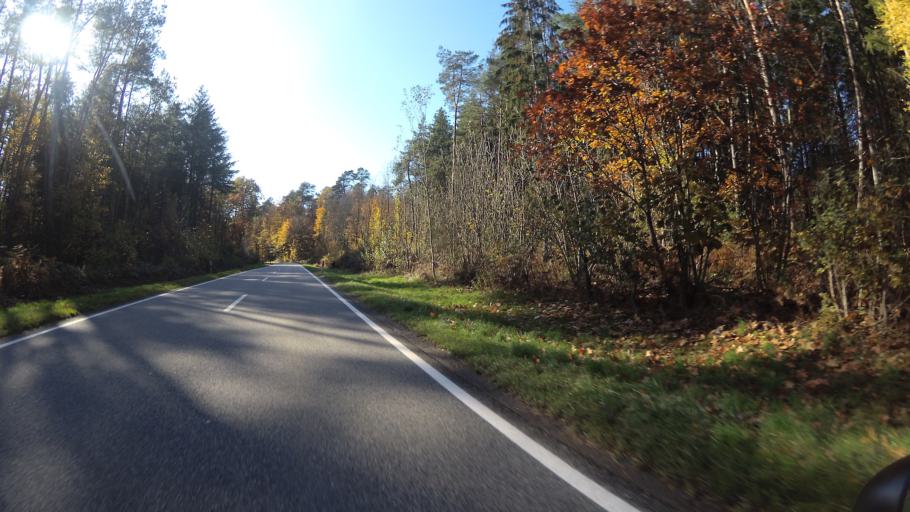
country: DE
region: Saarland
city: Losheim
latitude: 49.4938
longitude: 6.7207
